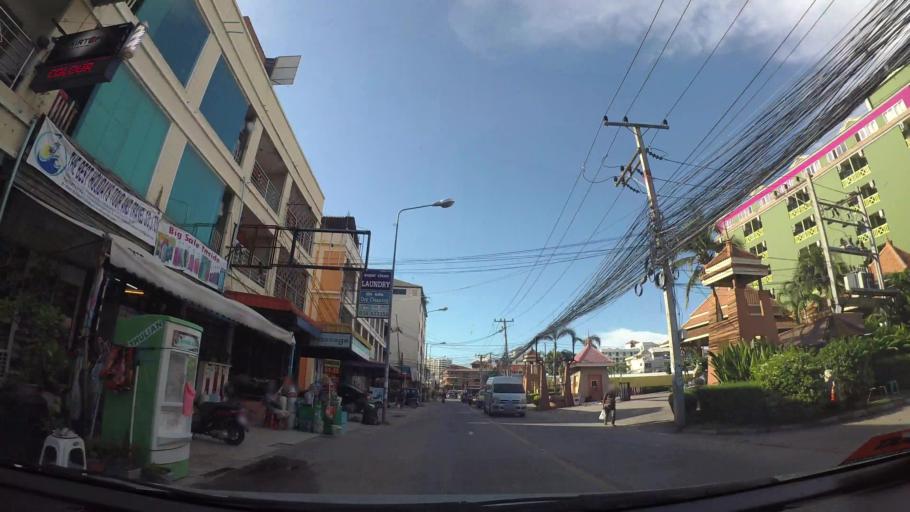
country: TH
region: Chon Buri
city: Phatthaya
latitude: 12.9192
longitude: 100.8786
